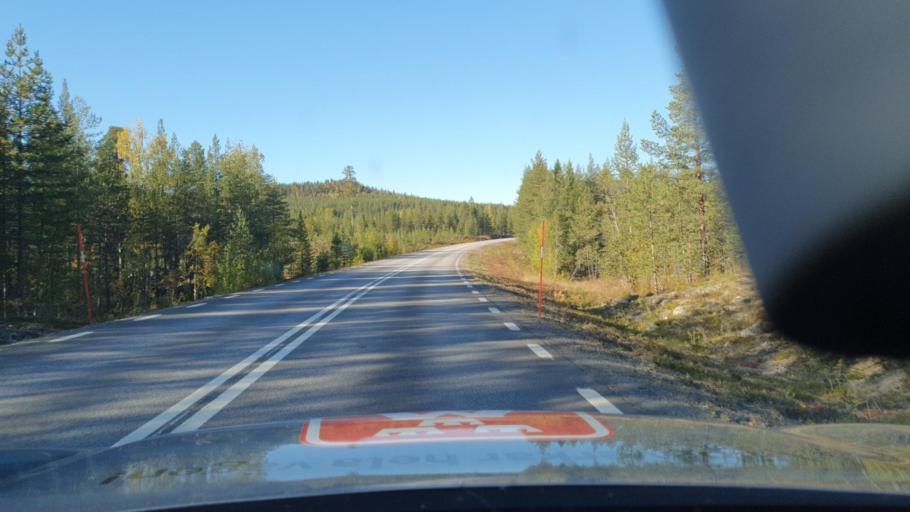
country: SE
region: Norrbotten
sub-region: Arvidsjaurs Kommun
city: Arvidsjaur
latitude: 65.6823
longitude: 20.0182
